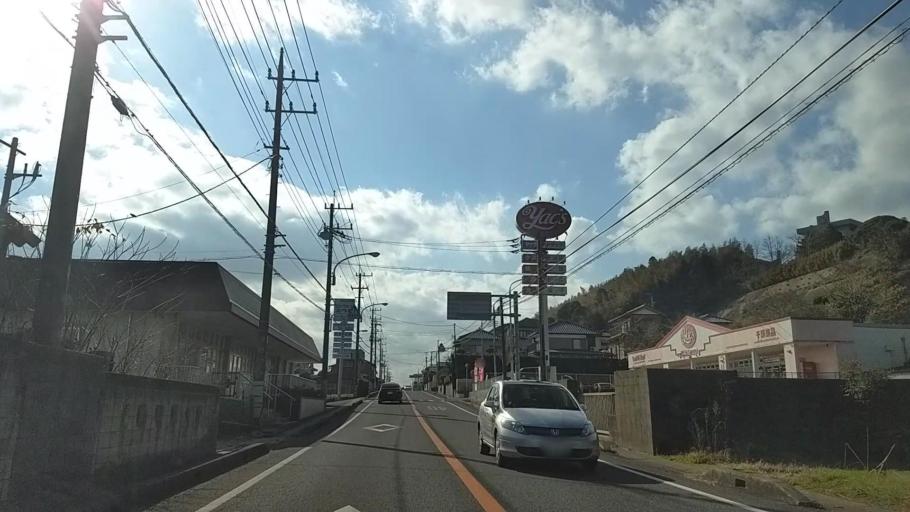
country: JP
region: Chiba
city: Naruto
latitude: 35.6369
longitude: 140.4539
